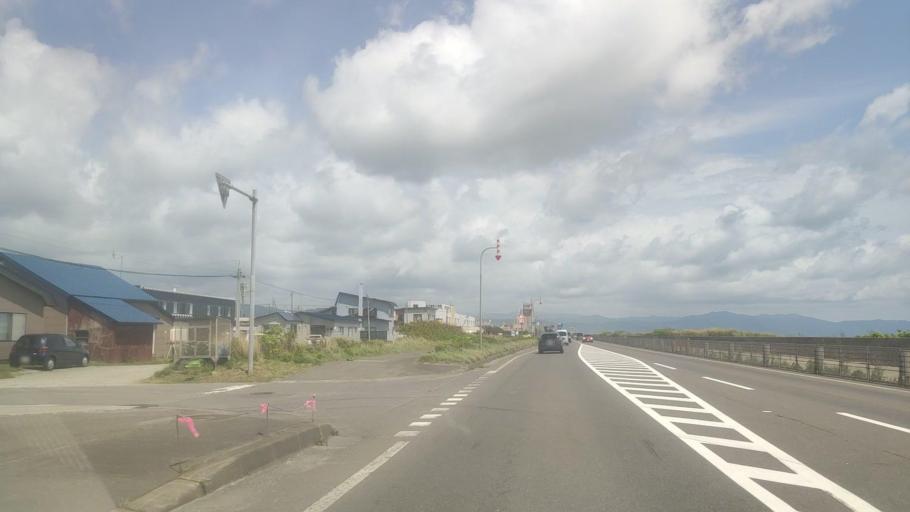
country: JP
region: Hokkaido
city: Niseko Town
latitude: 42.5081
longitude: 140.3757
